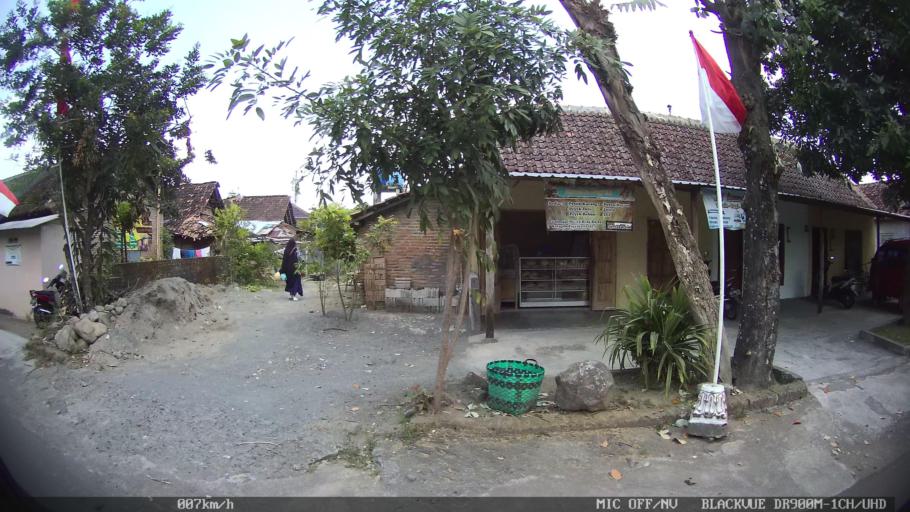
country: ID
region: Daerah Istimewa Yogyakarta
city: Yogyakarta
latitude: -7.8208
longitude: 110.4019
